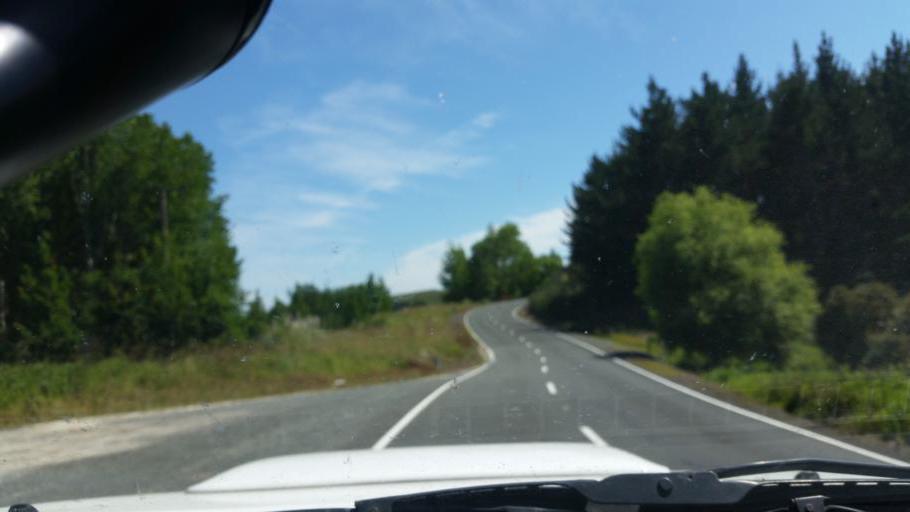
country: NZ
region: Auckland
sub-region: Auckland
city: Wellsford
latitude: -36.2092
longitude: 174.3918
